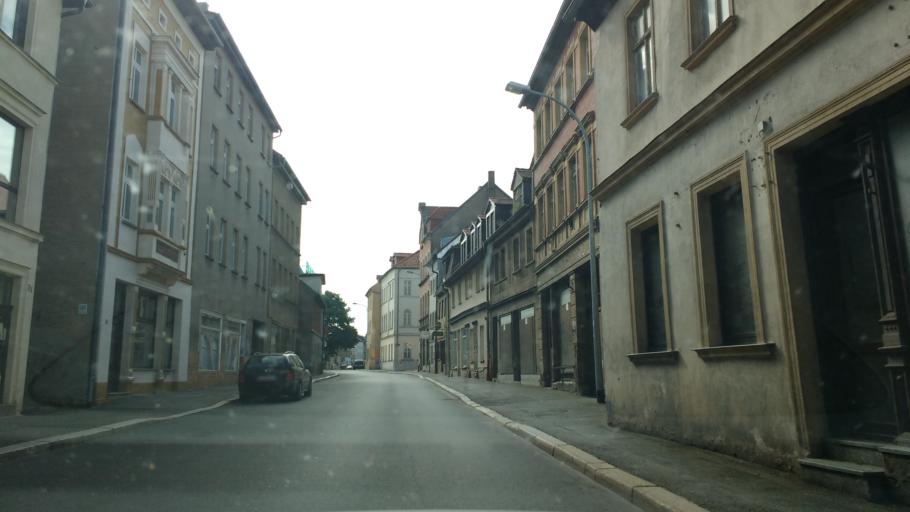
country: DE
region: Saxony-Anhalt
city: Zeitz
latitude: 51.0484
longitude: 12.1365
